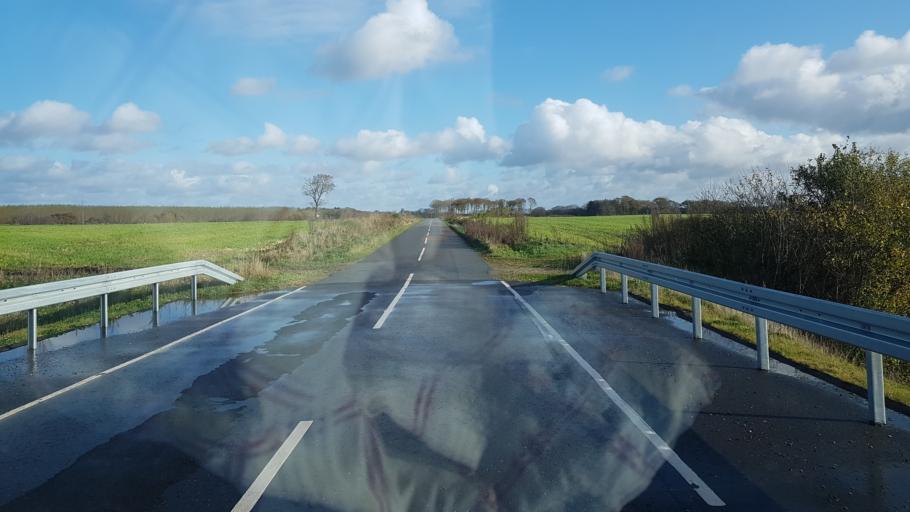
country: DK
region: South Denmark
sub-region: Varde Kommune
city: Olgod
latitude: 55.6910
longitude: 8.6918
